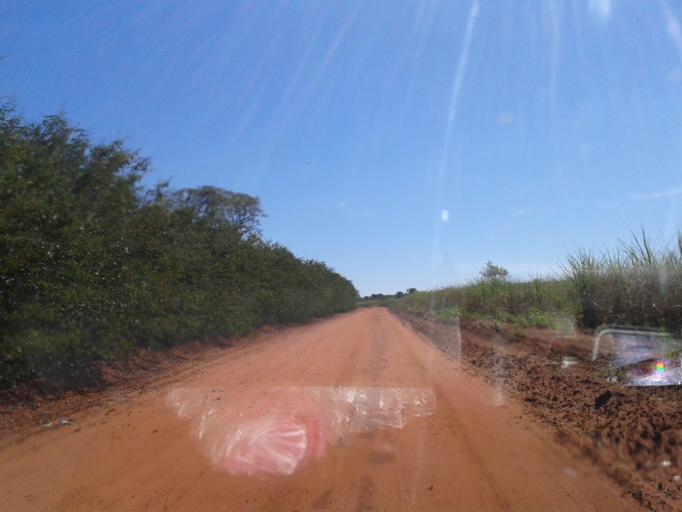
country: BR
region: Minas Gerais
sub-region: Santa Vitoria
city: Santa Vitoria
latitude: -19.0246
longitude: -50.3653
